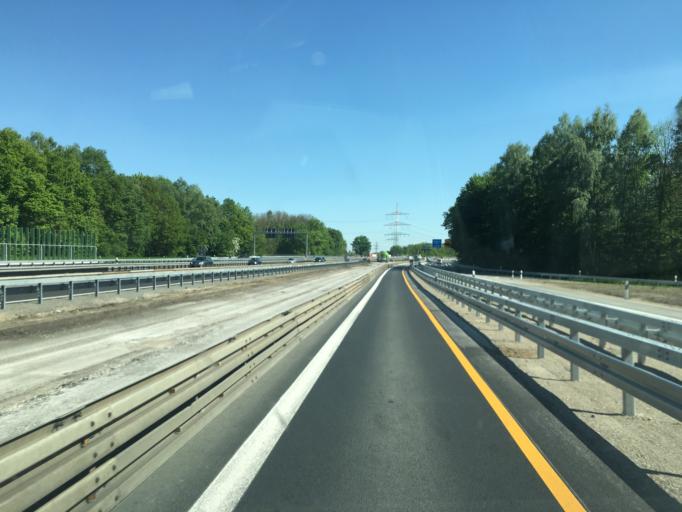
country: DE
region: North Rhine-Westphalia
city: Castrop-Rauxel
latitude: 51.5200
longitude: 7.3833
